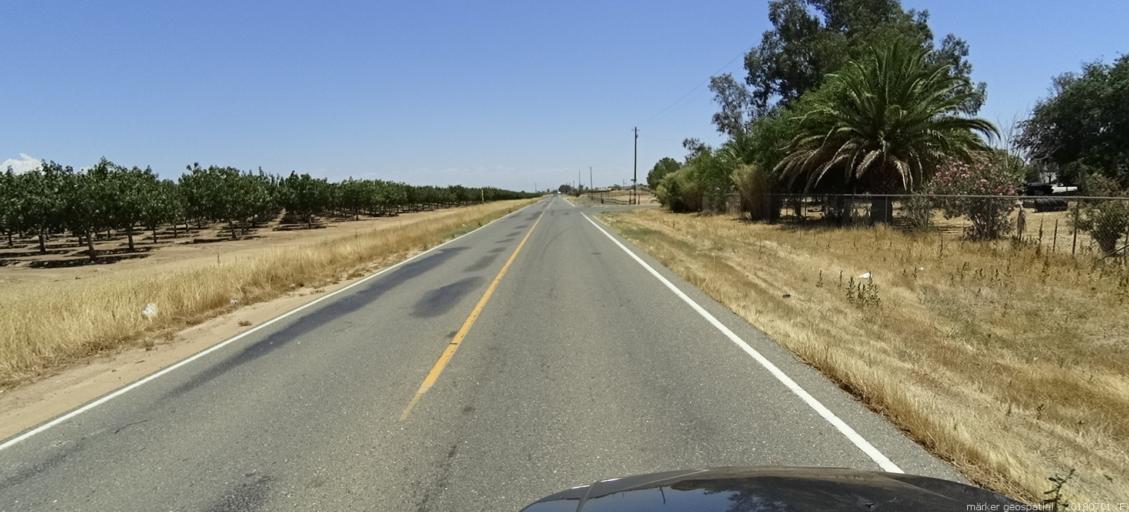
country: US
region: California
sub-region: Madera County
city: Madera Acres
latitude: 37.0541
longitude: -119.9998
